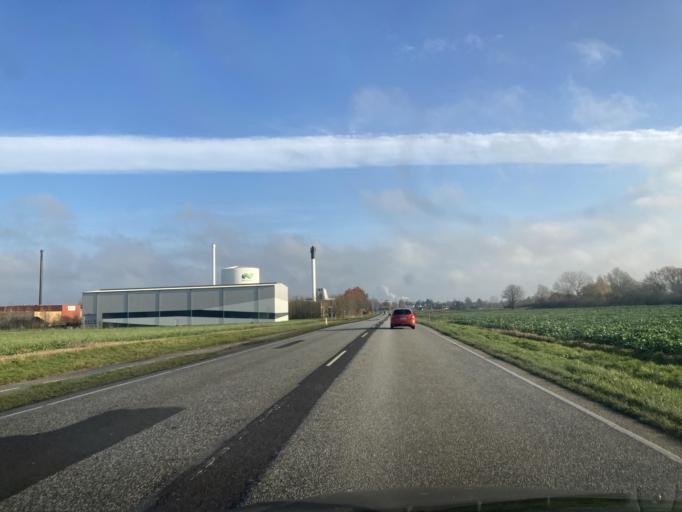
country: DK
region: Zealand
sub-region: Guldborgsund Kommune
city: Nykobing Falster
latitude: 54.7569
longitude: 11.8218
